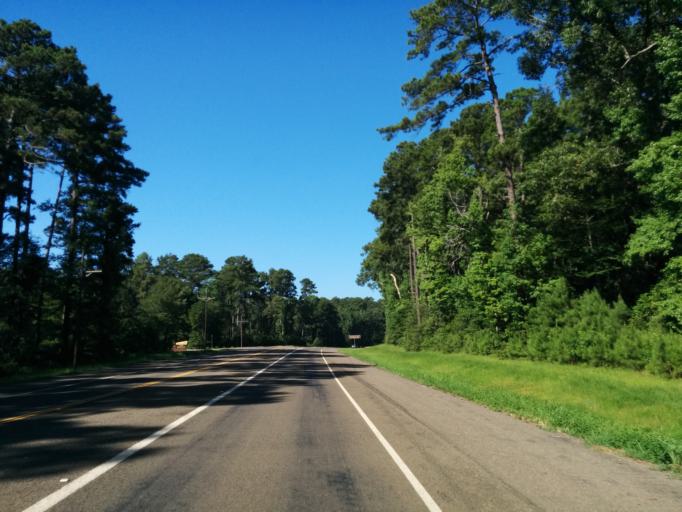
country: US
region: Texas
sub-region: Sabine County
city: Milam
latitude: 31.4459
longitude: -93.7683
